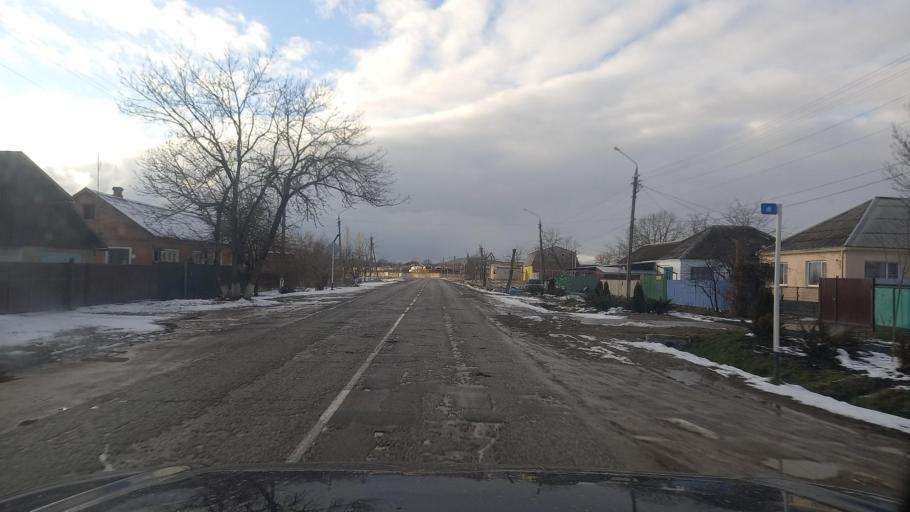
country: RU
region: Krasnodarskiy
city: Smolenskaya
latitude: 44.7766
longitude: 38.8362
